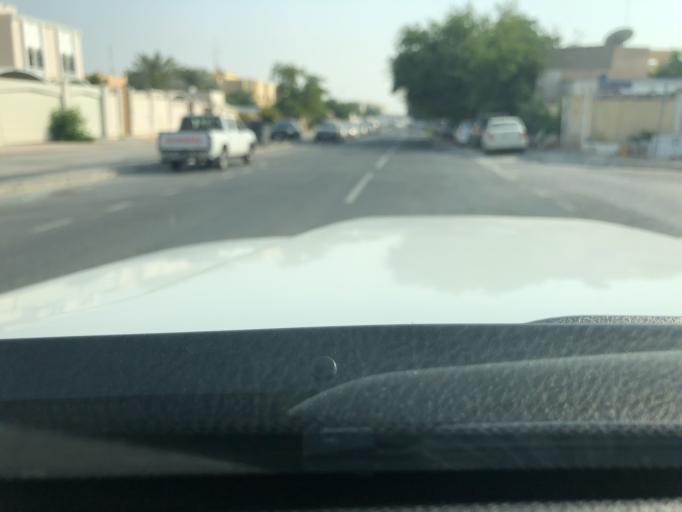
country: QA
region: Baladiyat ar Rayyan
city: Ar Rayyan
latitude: 25.3265
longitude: 51.4747
